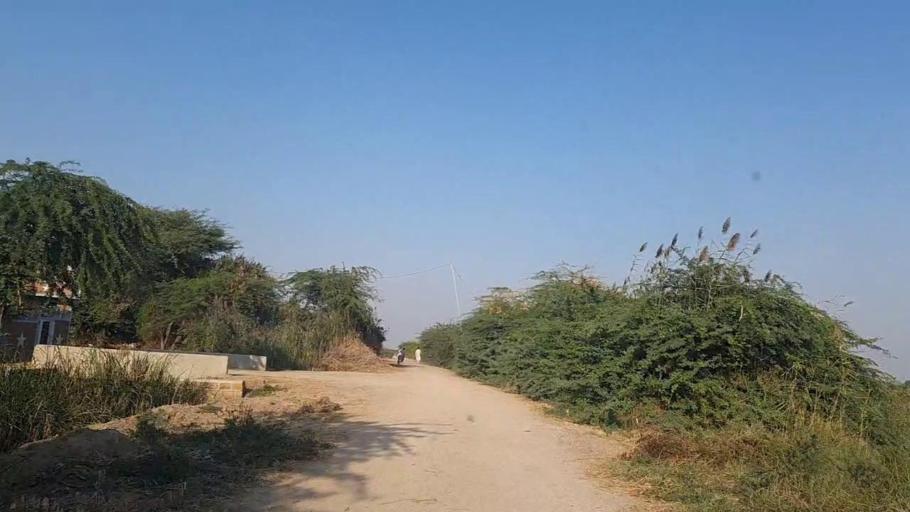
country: PK
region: Sindh
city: Thatta
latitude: 24.7212
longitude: 67.9454
